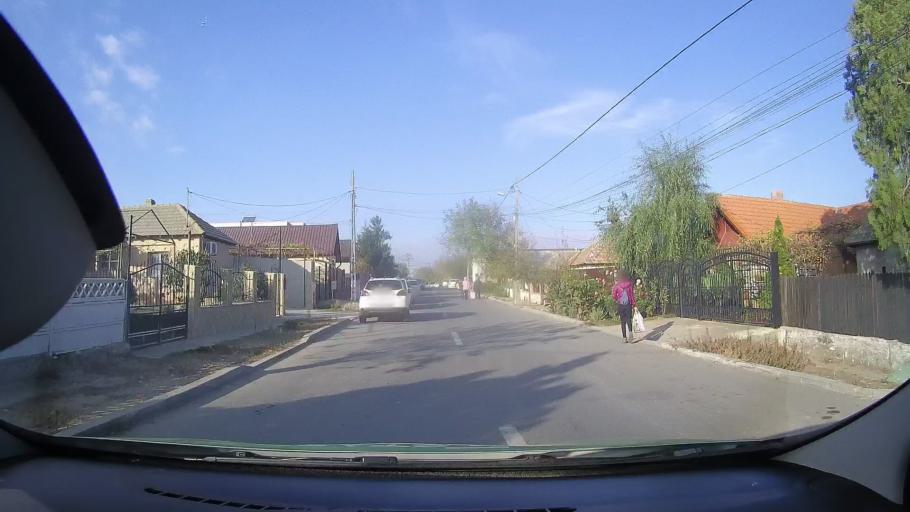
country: RO
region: Constanta
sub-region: Comuna Lumina
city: Lumina
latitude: 44.2864
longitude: 28.5648
